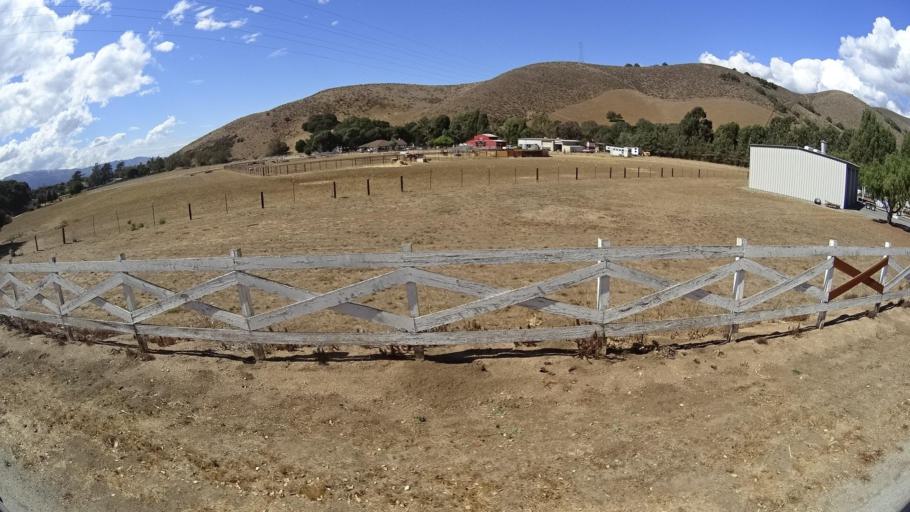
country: US
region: California
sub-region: Monterey County
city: Chualar
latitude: 36.5986
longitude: -121.4349
